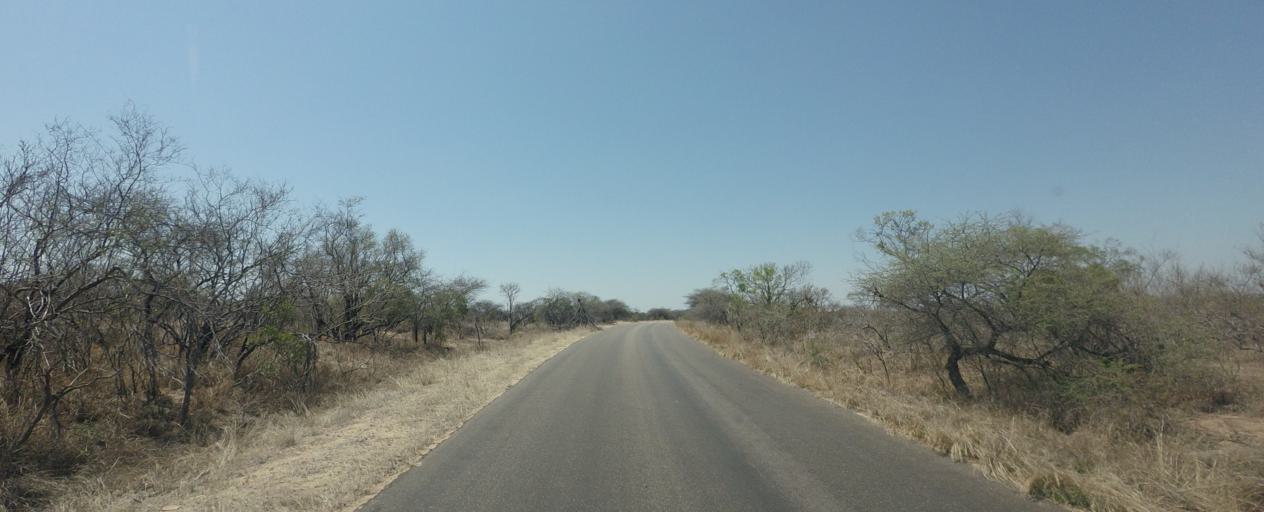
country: ZA
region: Limpopo
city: Thulamahashi
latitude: -24.4383
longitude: 31.4904
